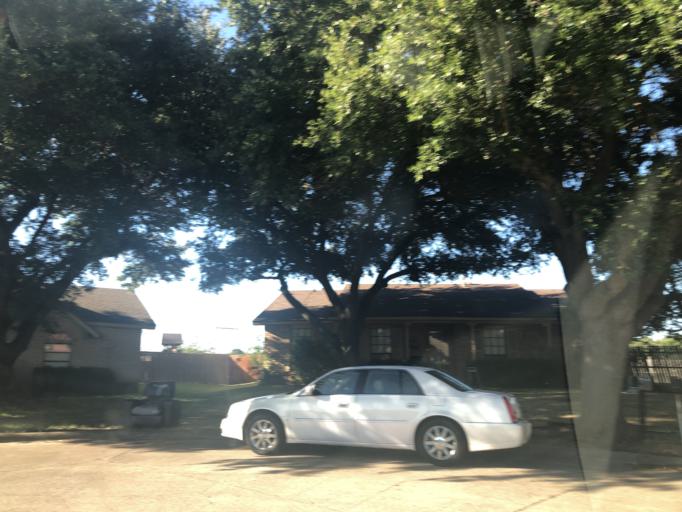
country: US
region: Texas
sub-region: Dallas County
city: Duncanville
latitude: 32.6367
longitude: -96.9502
